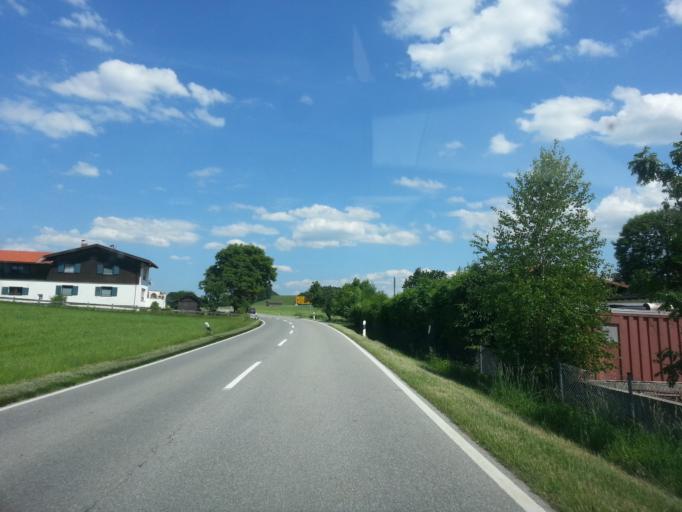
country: DE
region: Bavaria
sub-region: Upper Bavaria
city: Irschenberg
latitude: 47.8054
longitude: 11.9244
